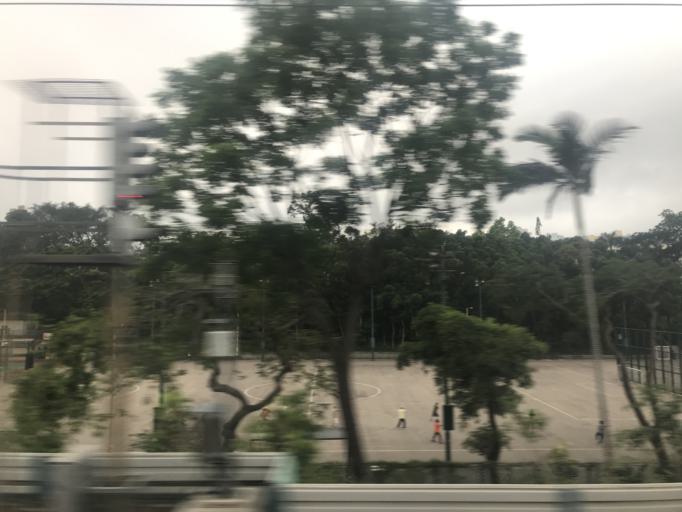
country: HK
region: Kowloon City
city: Kowloon
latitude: 22.3277
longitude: 114.1750
